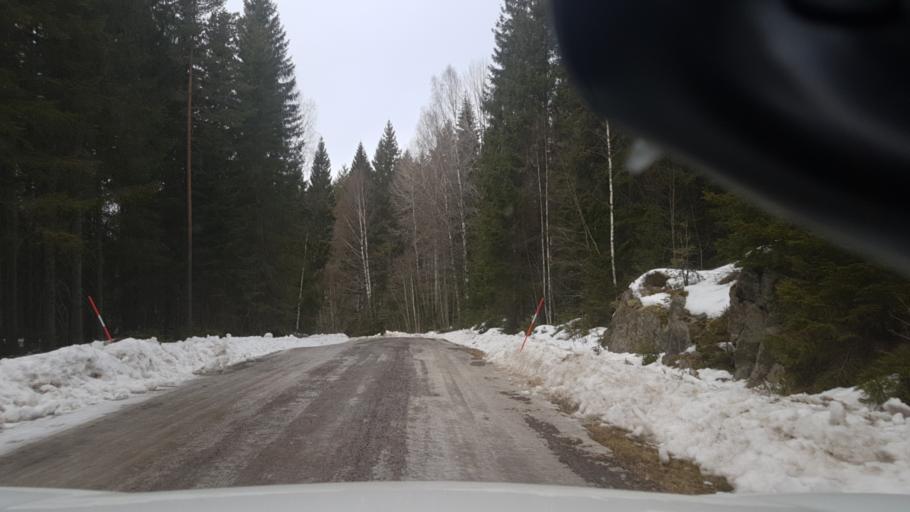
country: SE
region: Vaermland
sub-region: Eda Kommun
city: Amotfors
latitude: 59.8192
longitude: 12.4542
